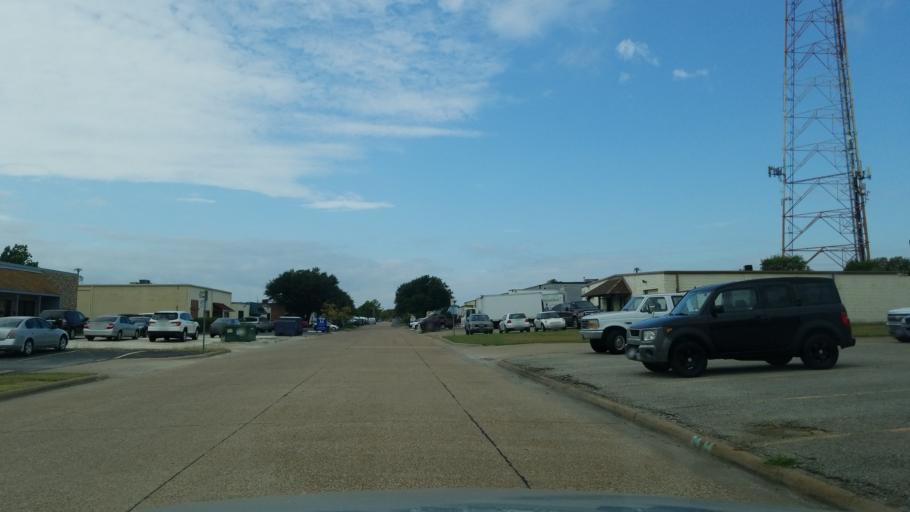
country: US
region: Texas
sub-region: Dallas County
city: Garland
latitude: 32.9003
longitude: -96.6856
